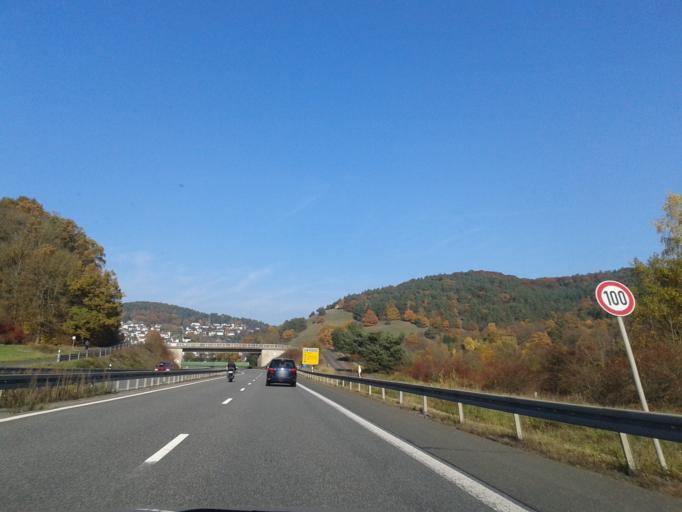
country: DE
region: Hesse
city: Herborn
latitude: 50.7119
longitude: 8.3044
